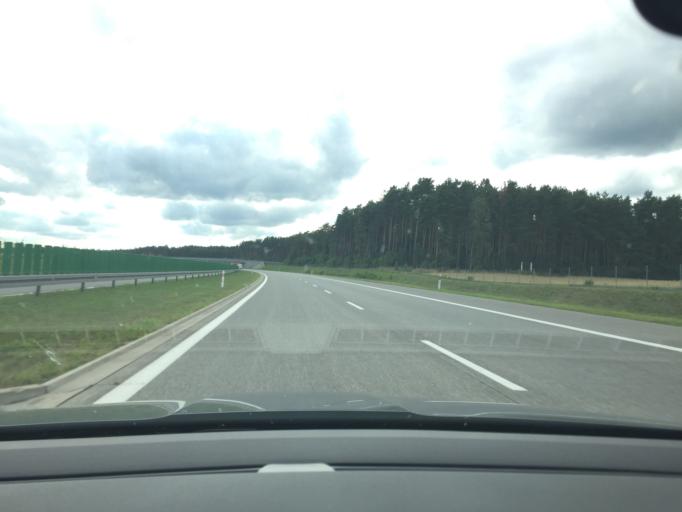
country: PL
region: Lubusz
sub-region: Powiat sulecinski
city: Torzym
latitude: 52.3379
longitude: 14.9594
